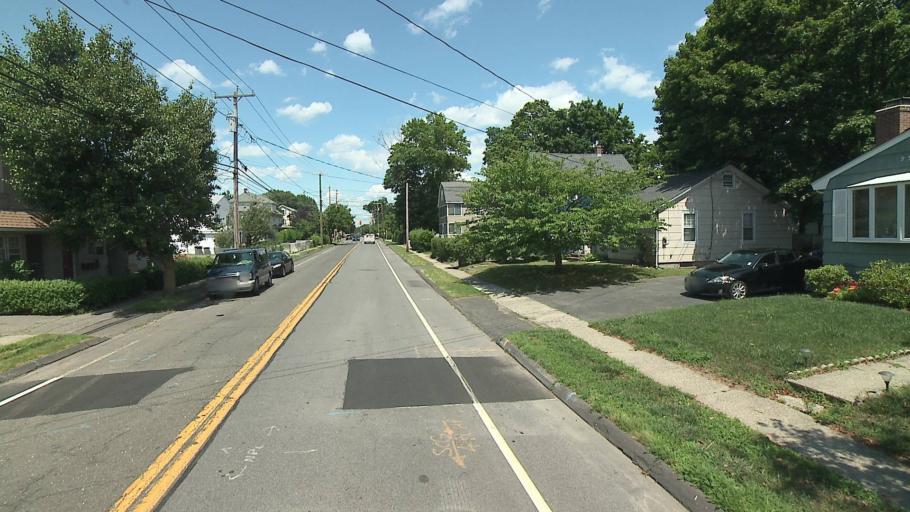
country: US
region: Connecticut
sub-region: New Haven County
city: Milford
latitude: 41.2092
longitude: -73.0578
